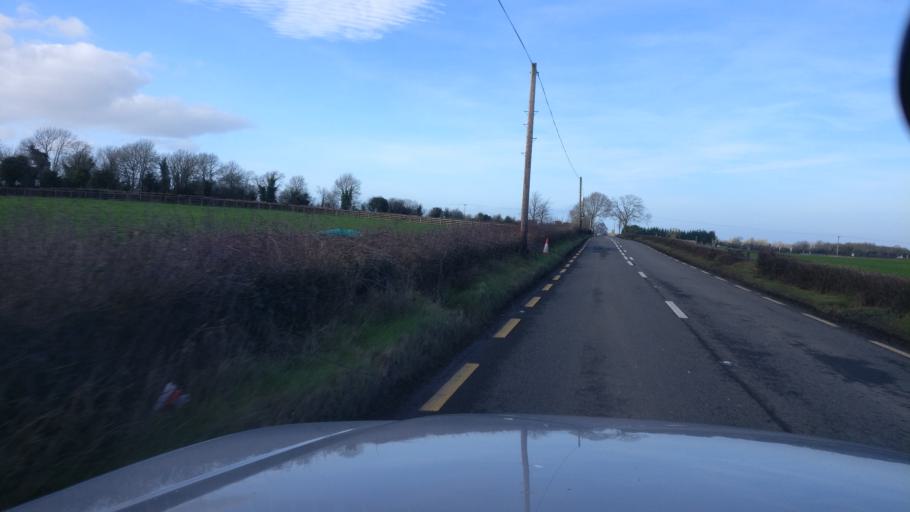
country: IE
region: Leinster
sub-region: Laois
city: Mountmellick
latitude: 53.0963
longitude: -7.3374
